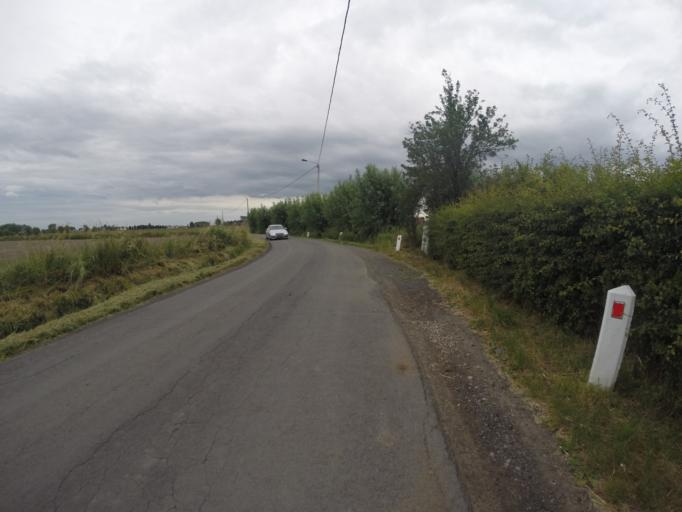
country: BE
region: Flanders
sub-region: Provincie West-Vlaanderen
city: Ruiselede
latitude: 51.0624
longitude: 3.3577
